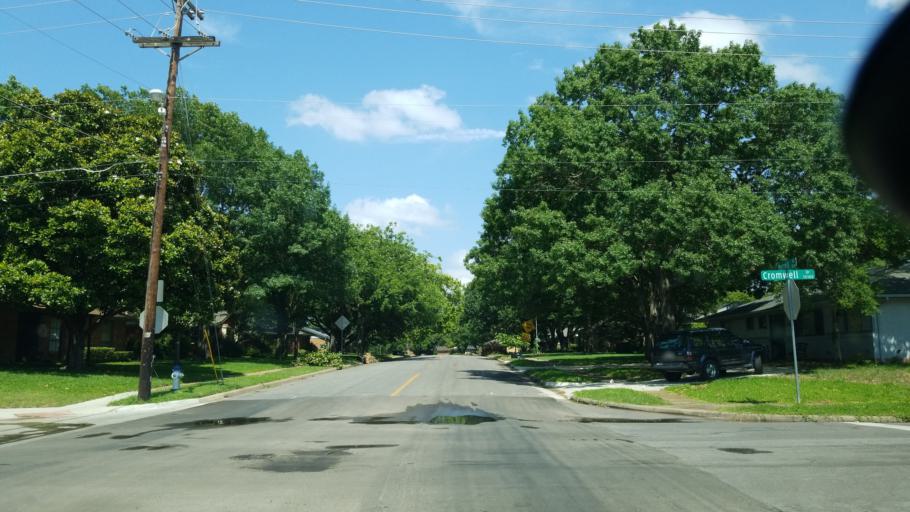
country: US
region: Texas
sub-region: Dallas County
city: Farmers Branch
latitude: 32.8875
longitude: -96.8627
